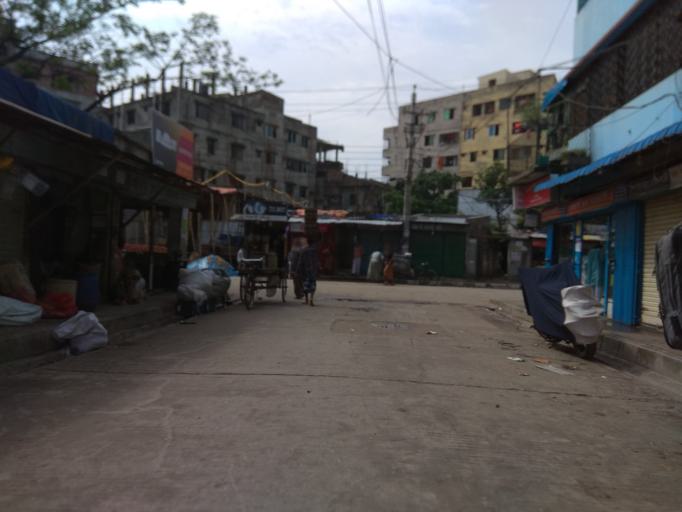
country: BD
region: Dhaka
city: Azimpur
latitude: 23.7987
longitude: 90.3554
